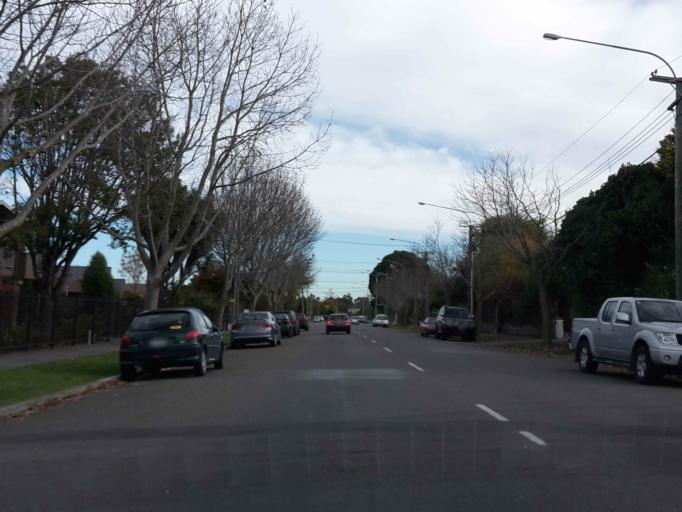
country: NZ
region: Canterbury
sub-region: Christchurch City
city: Christchurch
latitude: -43.5677
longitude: 172.6175
